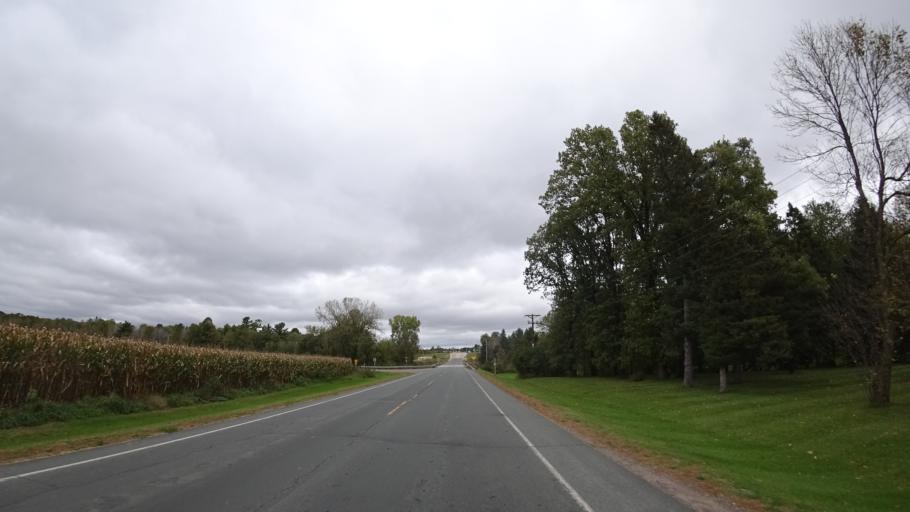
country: US
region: Wisconsin
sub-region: Saint Croix County
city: Woodville
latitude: 44.9293
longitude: -92.2783
